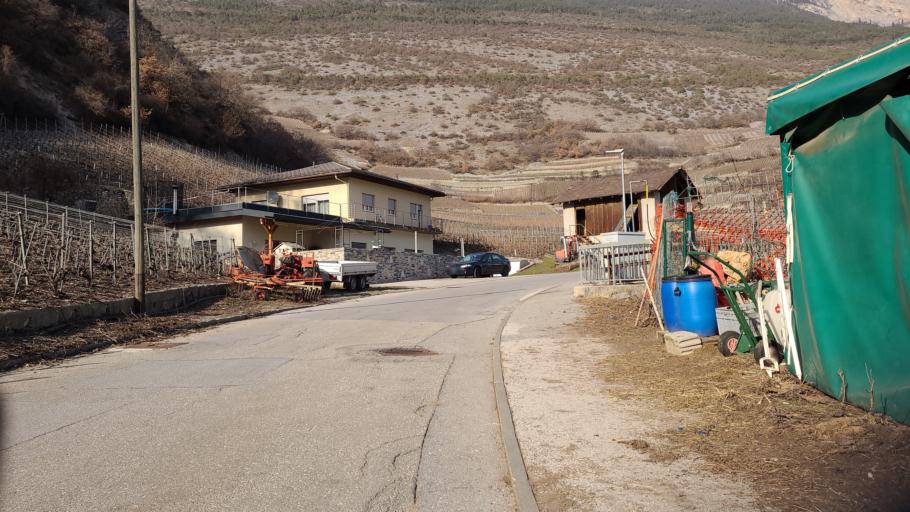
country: CH
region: Valais
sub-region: Leuk District
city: Salgesch
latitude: 46.3146
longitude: 7.5697
